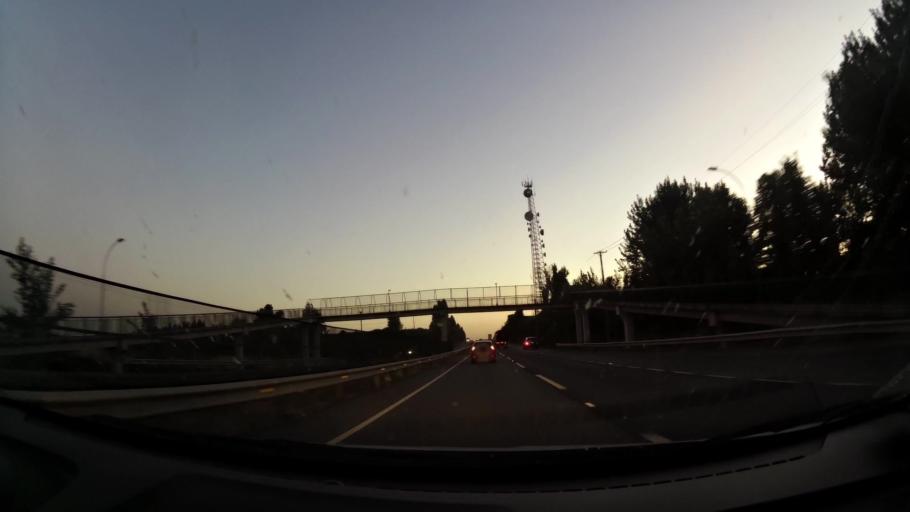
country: CL
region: Maule
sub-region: Provincia de Linares
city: Parral
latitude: -36.1440
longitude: -71.8103
